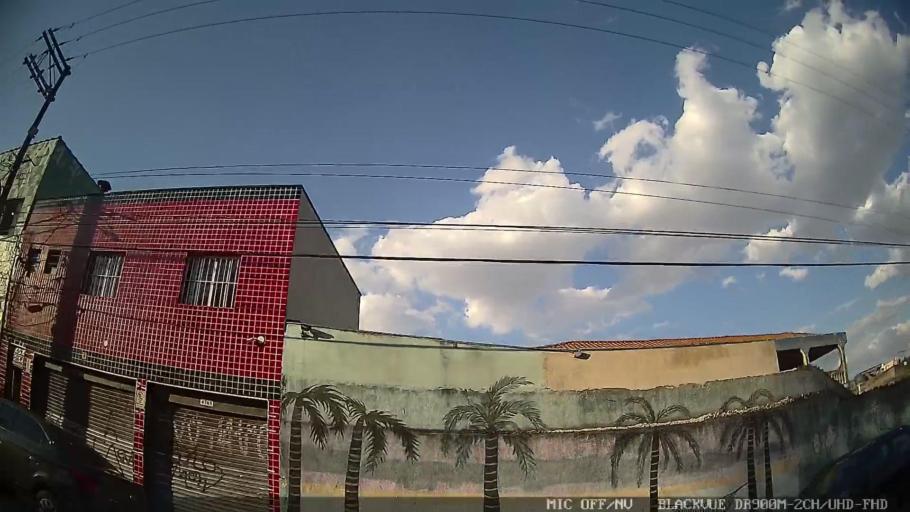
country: BR
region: Sao Paulo
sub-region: Sao Caetano Do Sul
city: Sao Caetano do Sul
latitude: -23.5785
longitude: -46.5437
